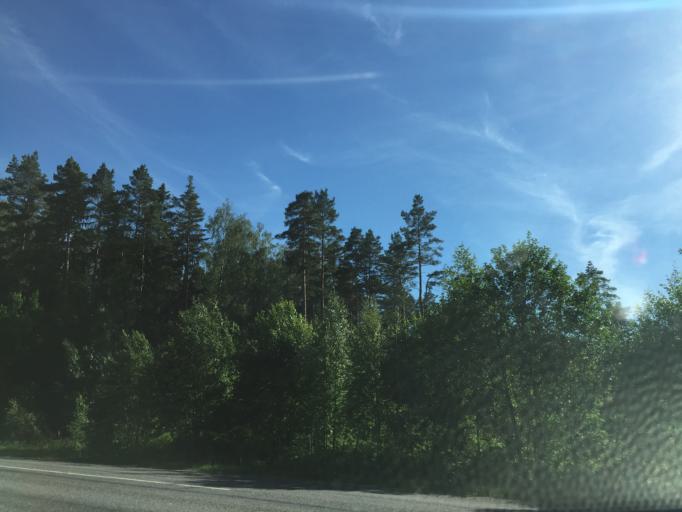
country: LV
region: Kuldigas Rajons
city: Kuldiga
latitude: 57.0617
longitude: 21.8132
